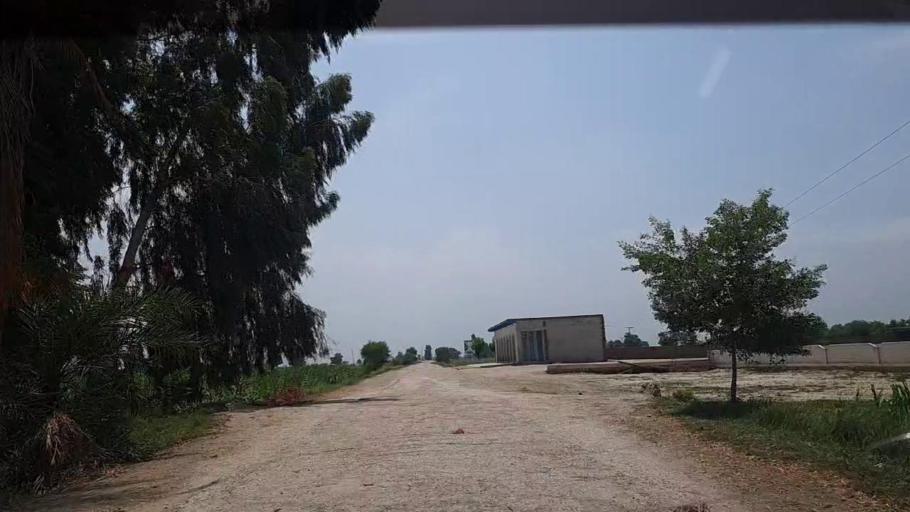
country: PK
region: Sindh
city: Khanpur
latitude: 27.9119
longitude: 69.3946
